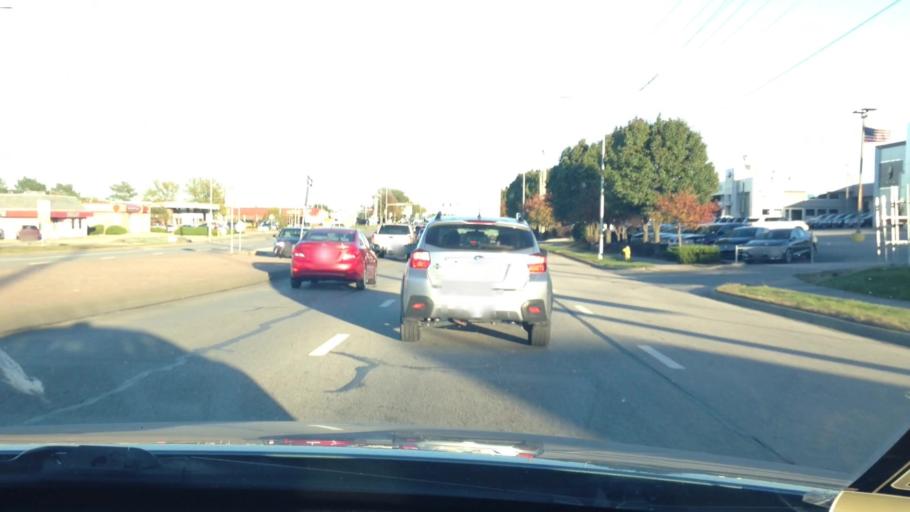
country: US
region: Kansas
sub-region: Johnson County
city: Olathe
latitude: 38.8836
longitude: -94.7877
